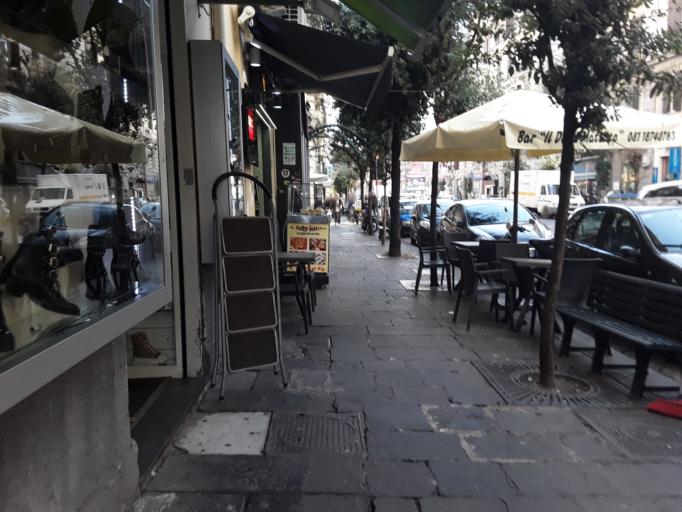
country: IT
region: Campania
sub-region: Provincia di Napoli
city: Napoli
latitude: 40.8569
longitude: 14.2673
